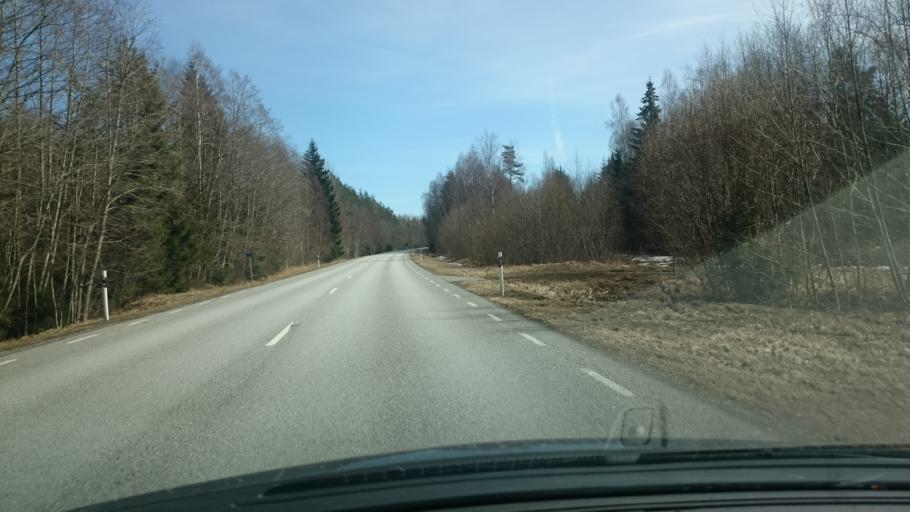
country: EE
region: Paernumaa
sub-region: Tootsi vald
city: Tootsi
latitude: 58.6641
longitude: 24.8088
